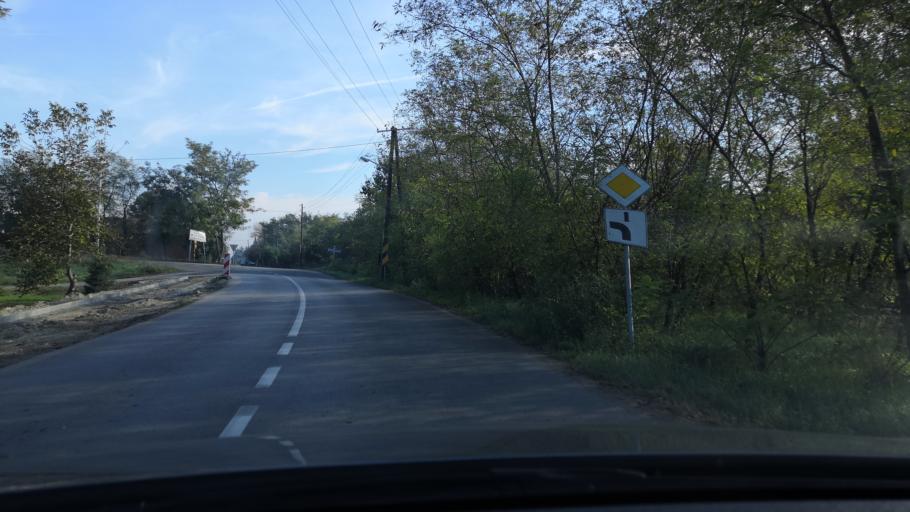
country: HU
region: Csongrad
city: Morahalom
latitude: 46.1264
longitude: 19.8524
